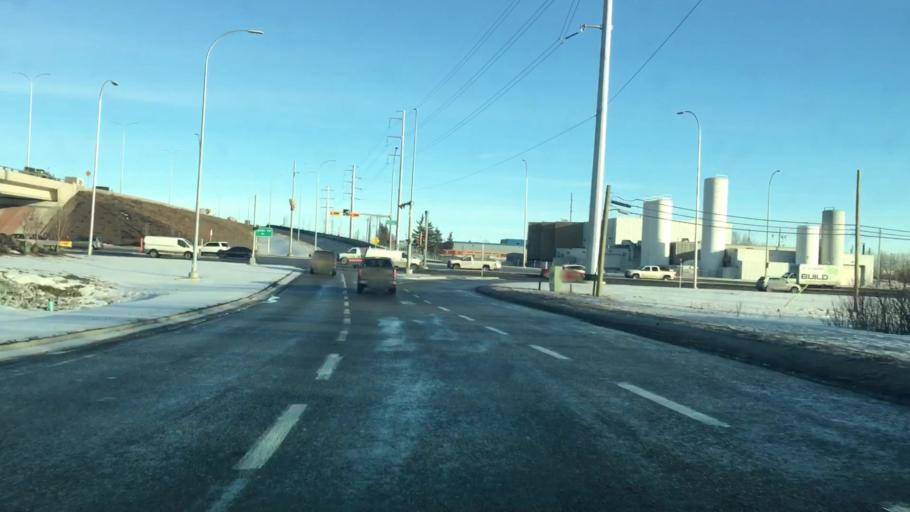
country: CA
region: Alberta
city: Calgary
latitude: 50.9786
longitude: -114.0002
